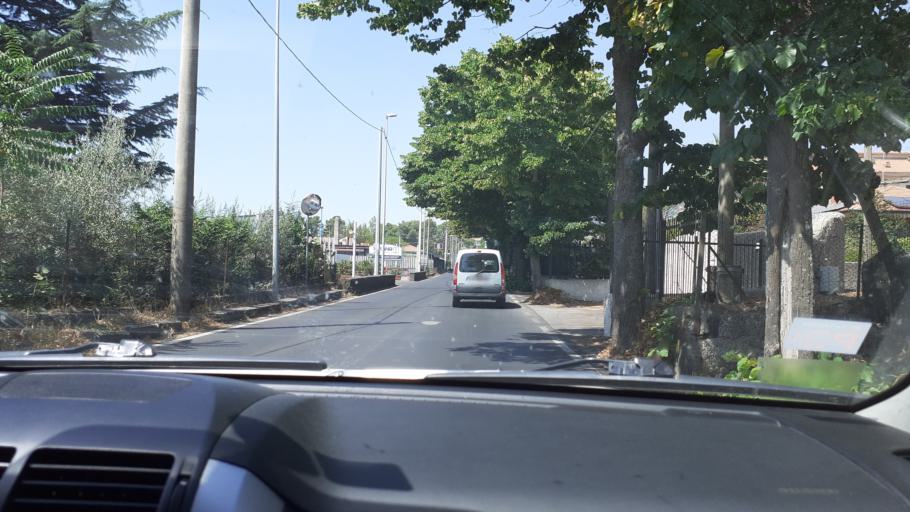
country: IT
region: Sicily
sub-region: Catania
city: Nicolosi
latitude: 37.6148
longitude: 15.0393
